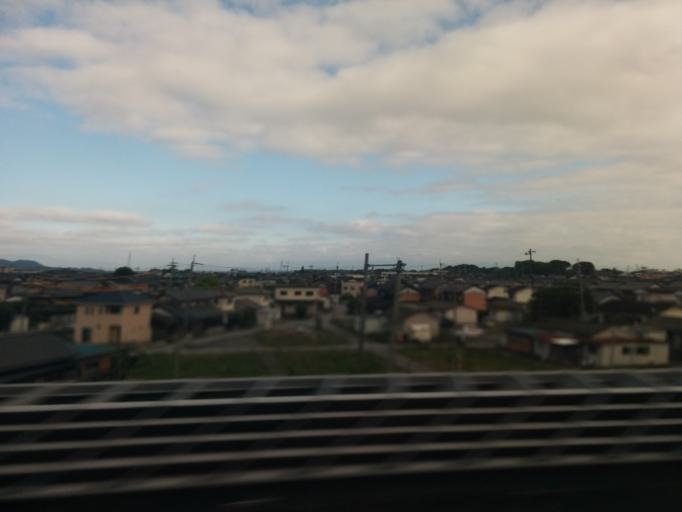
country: JP
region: Shiga Prefecture
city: Hikone
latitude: 35.2243
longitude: 136.2561
